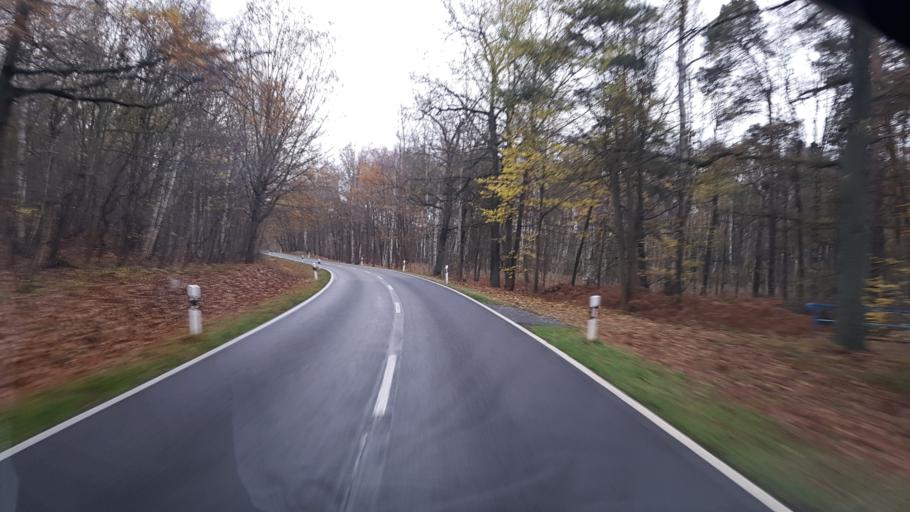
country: DE
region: Brandenburg
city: Lauchhammer
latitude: 51.5012
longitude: 13.7236
